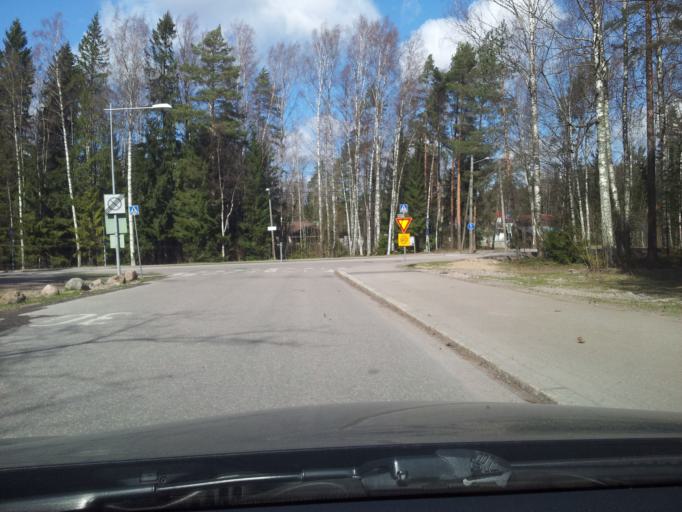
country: FI
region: Uusimaa
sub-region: Helsinki
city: Espoo
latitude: 60.1497
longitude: 24.6903
